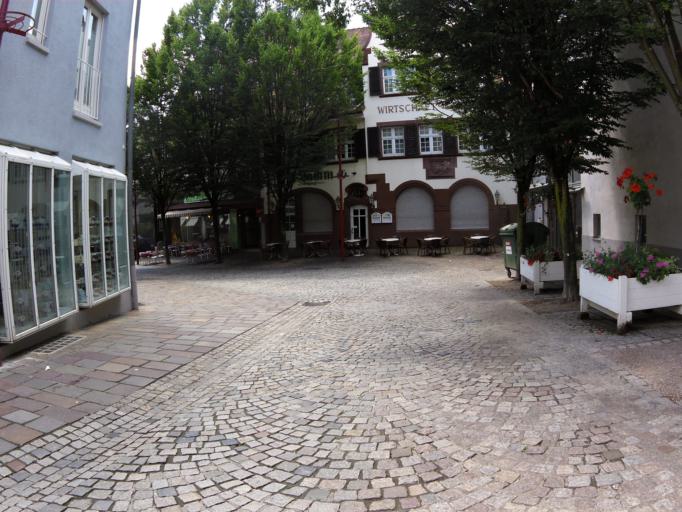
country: DE
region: Baden-Wuerttemberg
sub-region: Freiburg Region
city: Lahr
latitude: 48.3414
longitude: 7.8712
